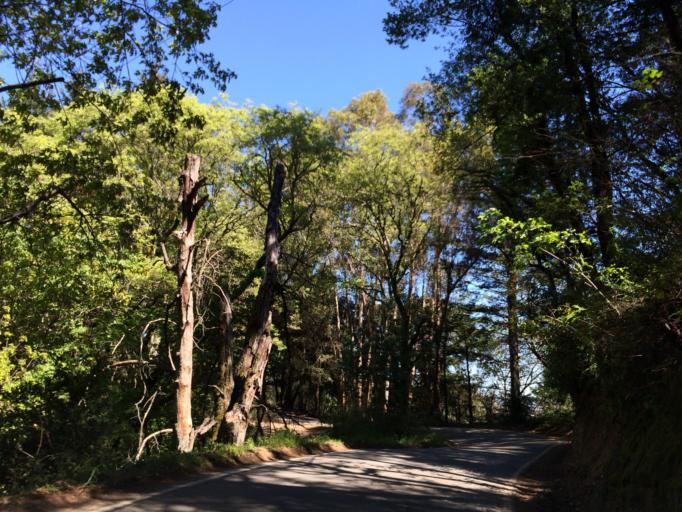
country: US
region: California
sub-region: Santa Clara County
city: Lexington Hills
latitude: 37.1727
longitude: -122.0265
